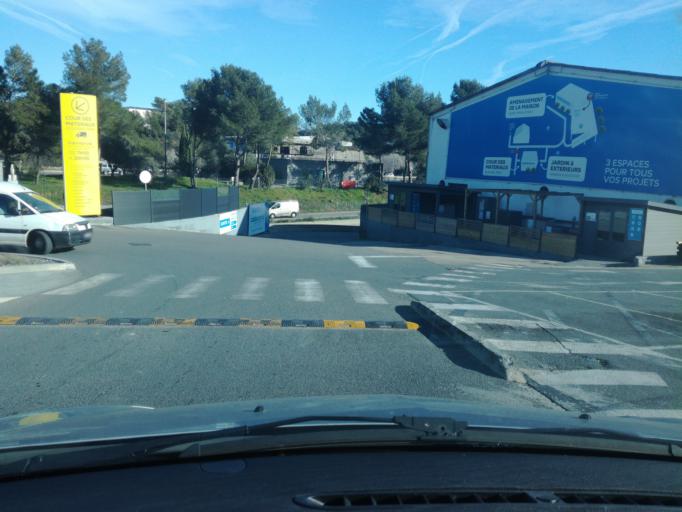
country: FR
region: Provence-Alpes-Cote d'Azur
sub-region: Departement des Alpes-Maritimes
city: Vallauris
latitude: 43.6022
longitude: 7.0713
